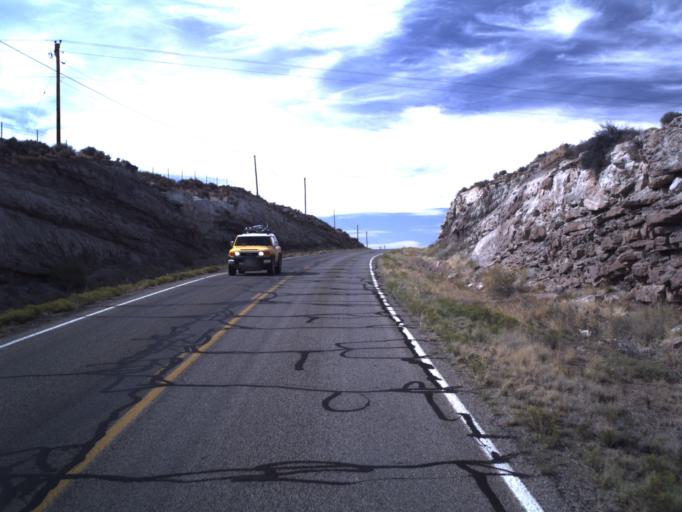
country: US
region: Utah
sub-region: San Juan County
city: Blanding
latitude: 37.2881
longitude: -109.2897
